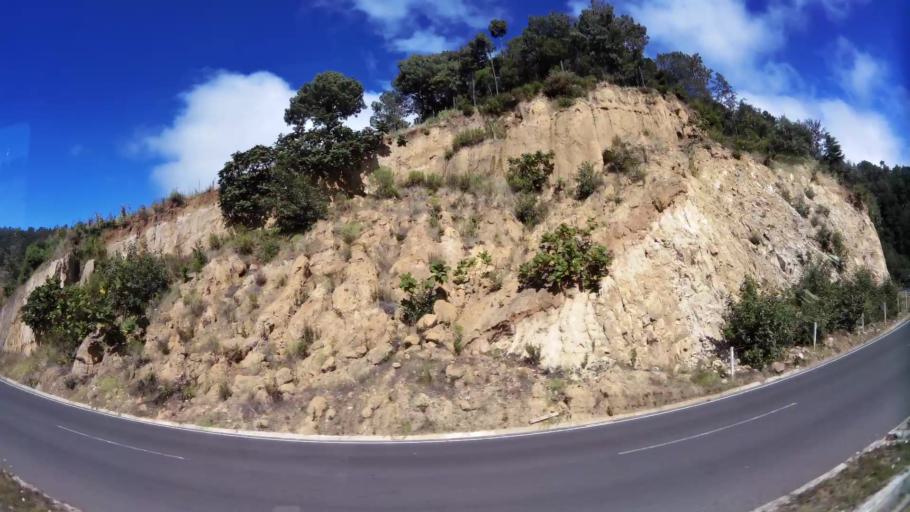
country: GT
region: Solola
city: Concepcion
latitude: 14.8359
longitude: -91.1813
